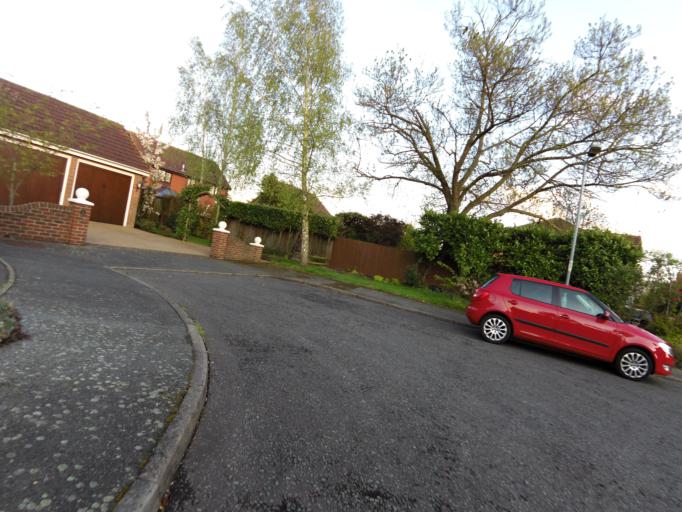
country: GB
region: England
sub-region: Suffolk
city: Ipswich
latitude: 52.0722
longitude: 1.1826
